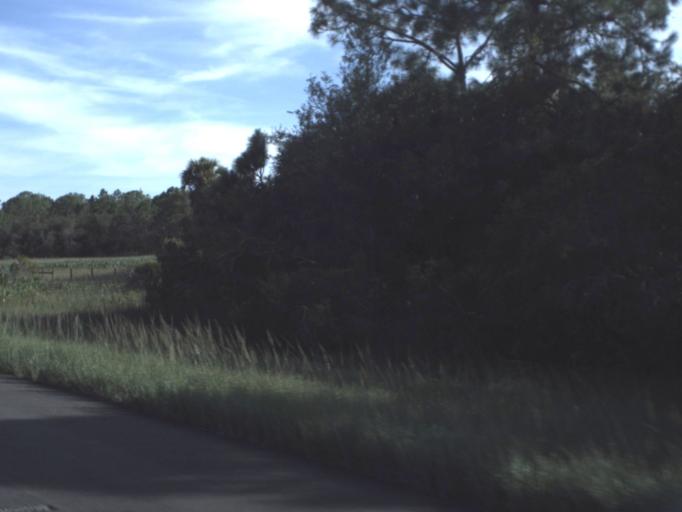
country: US
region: Florida
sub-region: Lee County
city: Suncoast Estates
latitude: 26.7943
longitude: -81.9099
